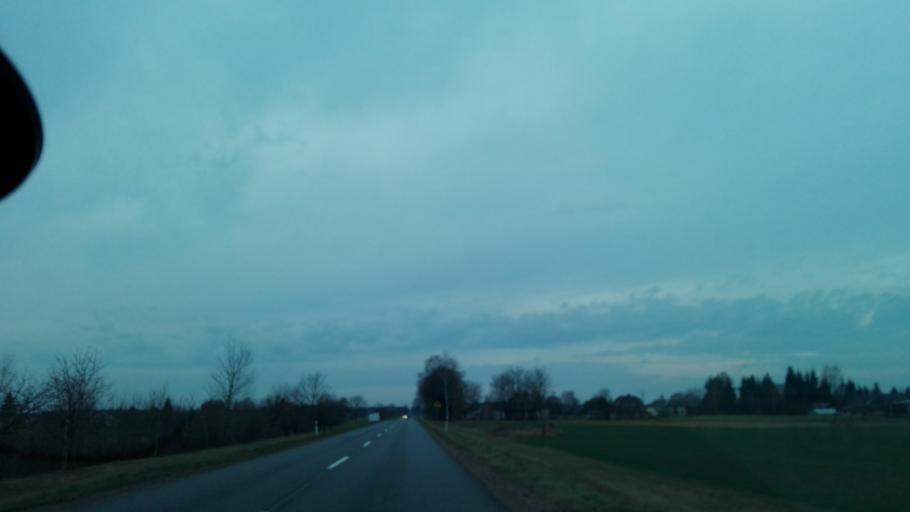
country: PL
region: Lublin Voivodeship
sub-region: Powiat radzynski
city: Komarowka Podlaska
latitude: 51.7763
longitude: 22.9273
